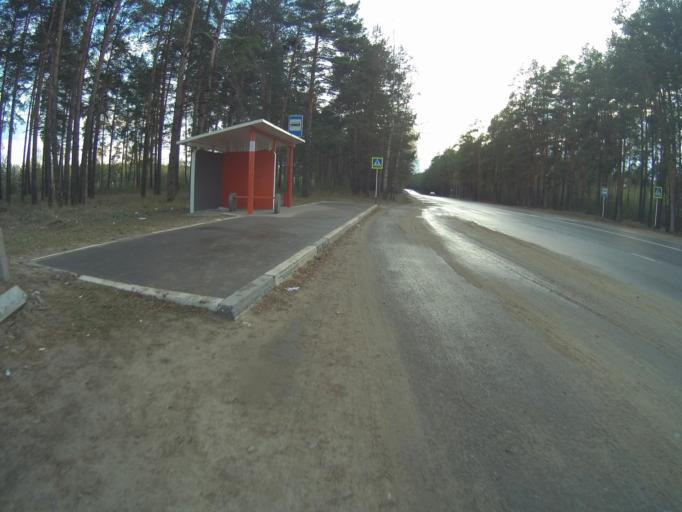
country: RU
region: Vladimir
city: Golovino
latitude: 56.0368
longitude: 40.4237
